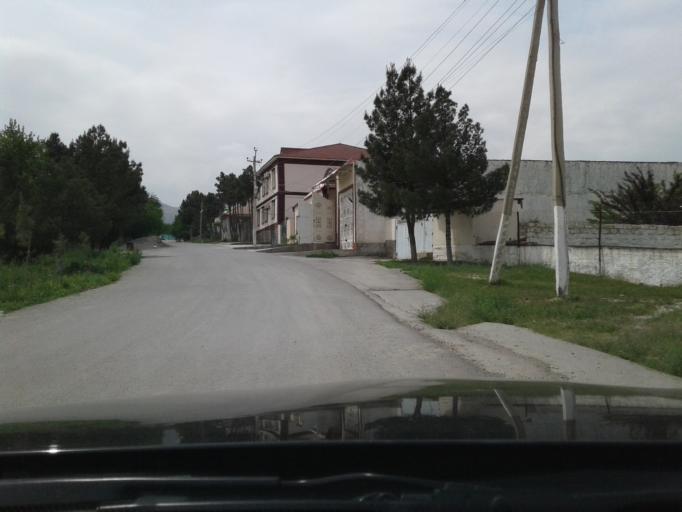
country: TM
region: Ahal
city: Abadan
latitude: 37.9598
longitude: 58.2220
